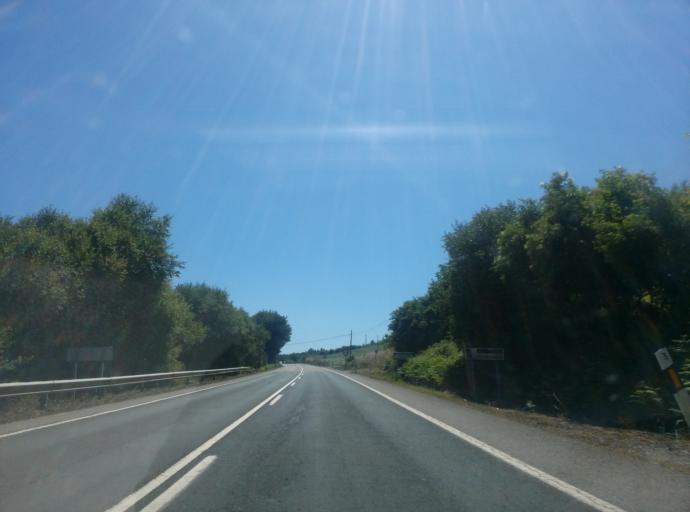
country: ES
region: Galicia
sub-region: Provincia de Lugo
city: Meira
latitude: 43.2077
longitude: -7.3272
